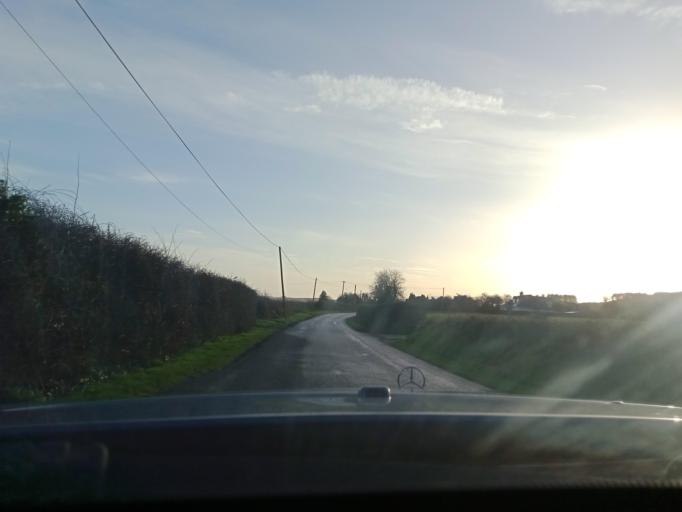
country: IE
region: Leinster
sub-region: Kilkenny
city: Callan
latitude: 52.4740
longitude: -7.4272
